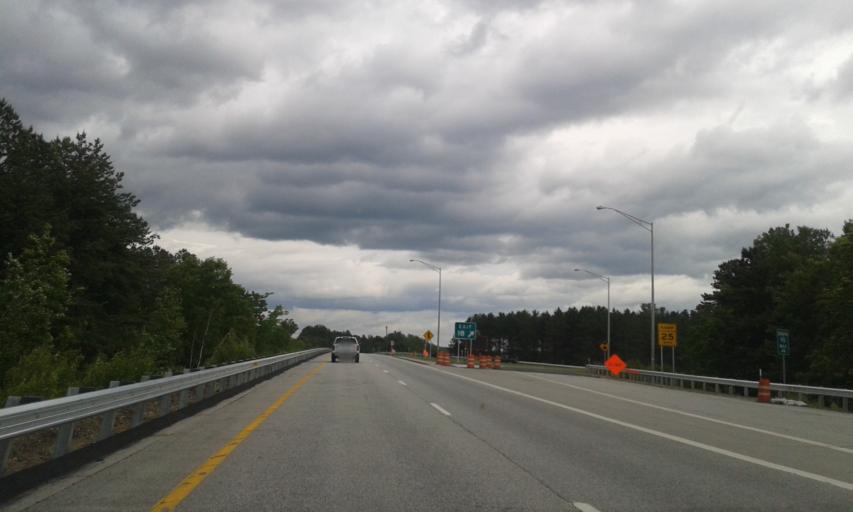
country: US
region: New Hampshire
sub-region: Merrimack County
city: Boscawen
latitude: 43.3332
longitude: -71.6085
